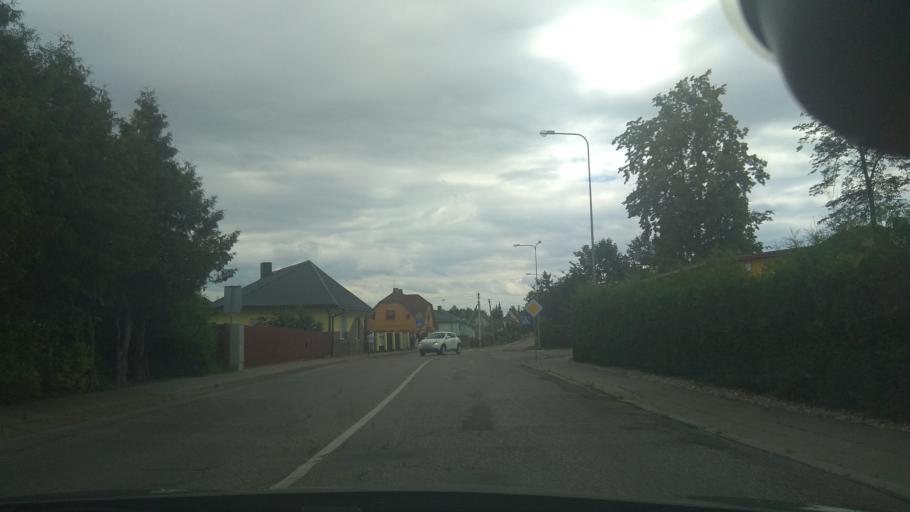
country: LT
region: Marijampoles apskritis
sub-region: Marijampole Municipality
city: Marijampole
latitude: 54.5496
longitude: 23.3539
